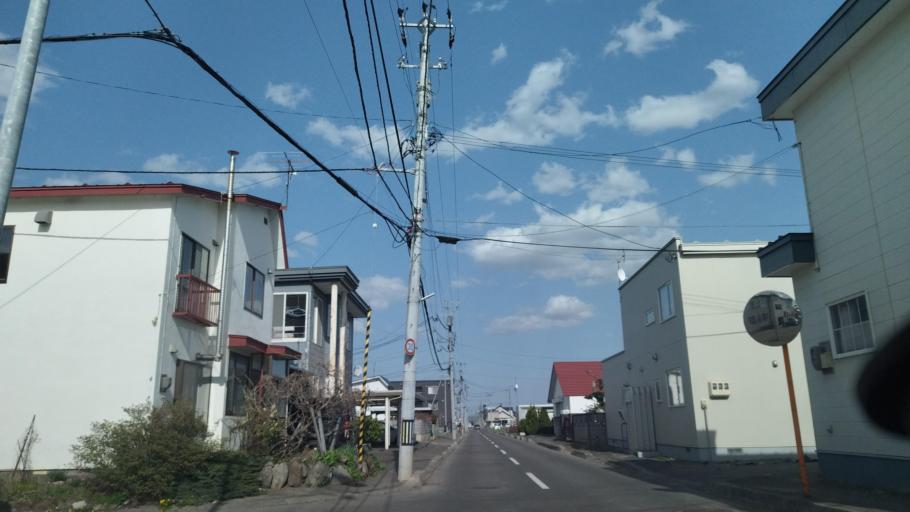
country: JP
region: Hokkaido
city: Obihiro
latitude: 42.9324
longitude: 143.1739
